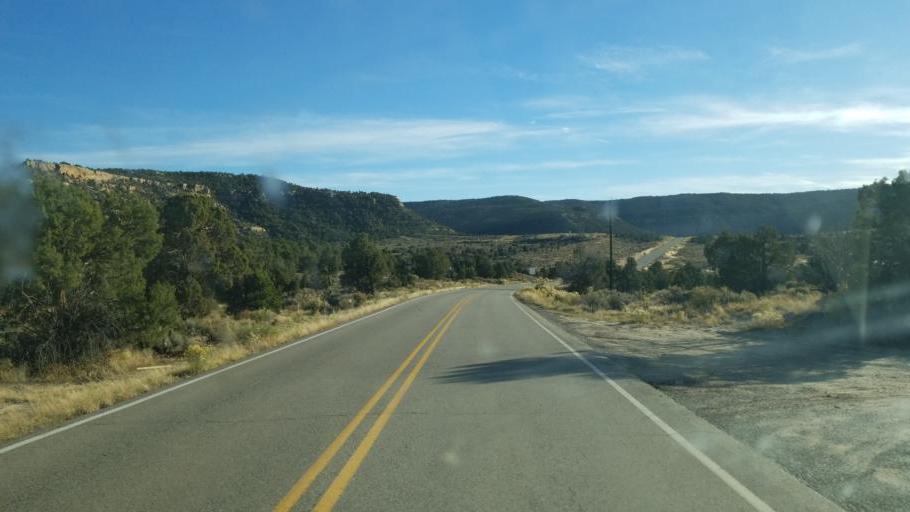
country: US
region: New Mexico
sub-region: San Juan County
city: Bloomfield
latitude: 36.7438
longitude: -107.6199
